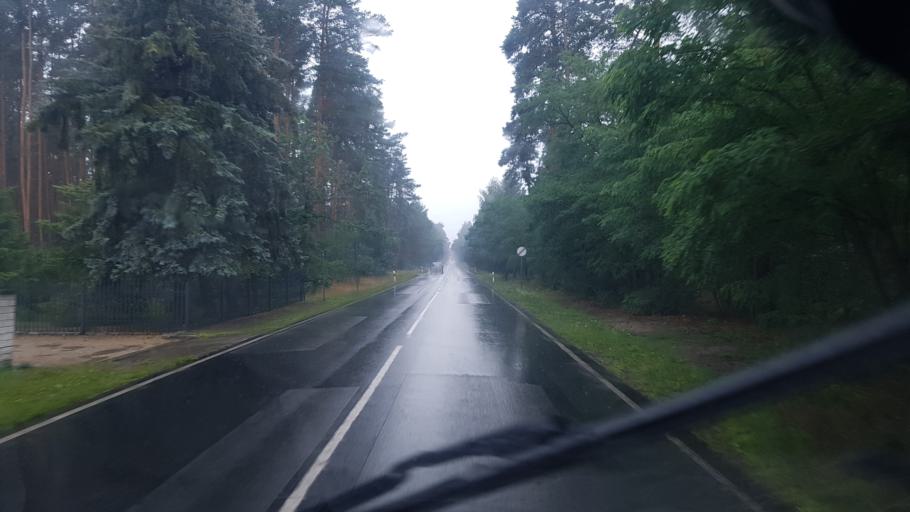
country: DE
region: Brandenburg
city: Baruth
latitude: 52.0581
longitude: 13.5463
